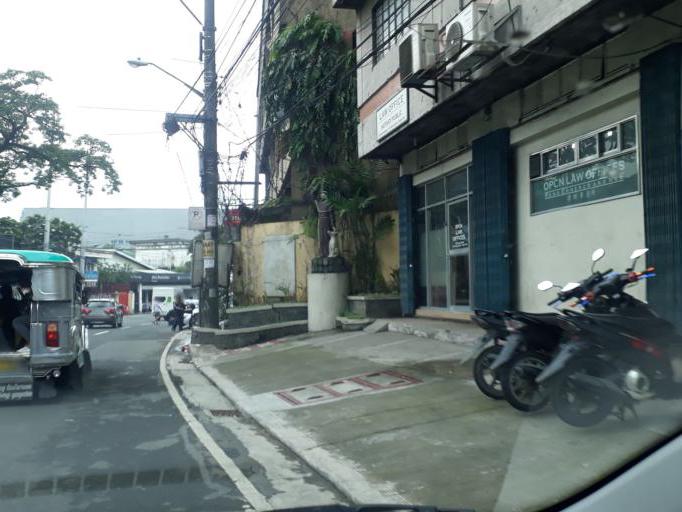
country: PH
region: Calabarzon
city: Del Monte
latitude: 14.6375
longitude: 121.0181
